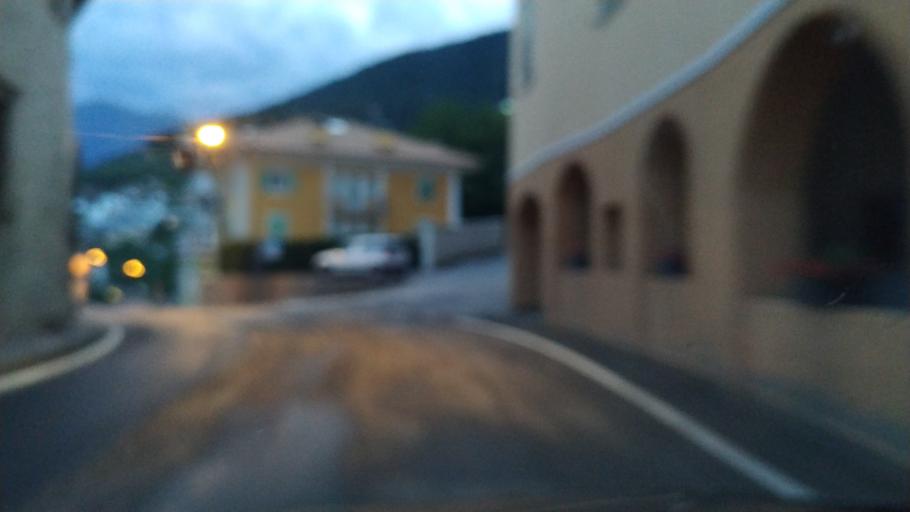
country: IT
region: Trentino-Alto Adige
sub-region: Provincia di Trento
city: Revo
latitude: 46.3911
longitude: 11.0573
